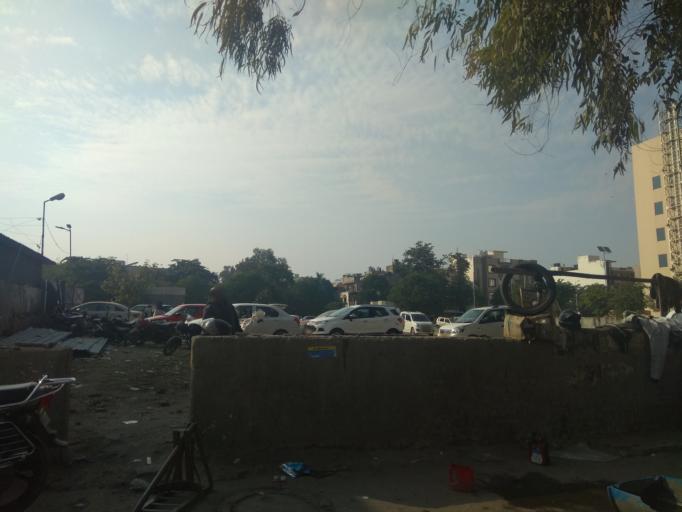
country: IN
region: NCT
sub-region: West Delhi
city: Nangloi Jat
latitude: 28.6307
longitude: 77.0685
